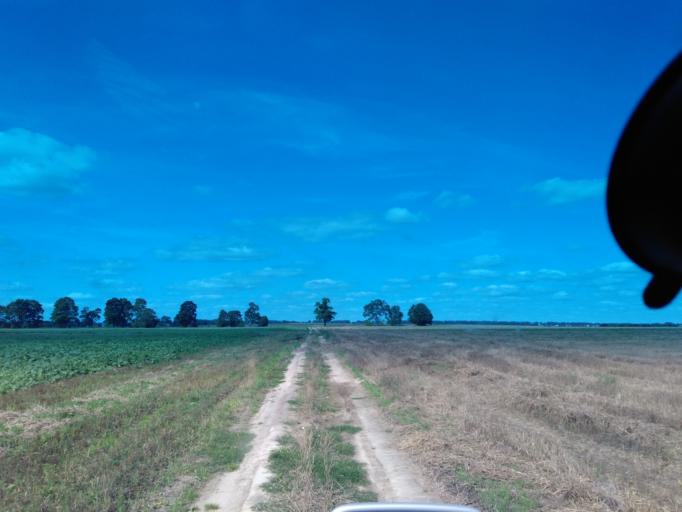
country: BY
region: Minsk
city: Stan'kava
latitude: 53.6317
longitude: 27.3266
